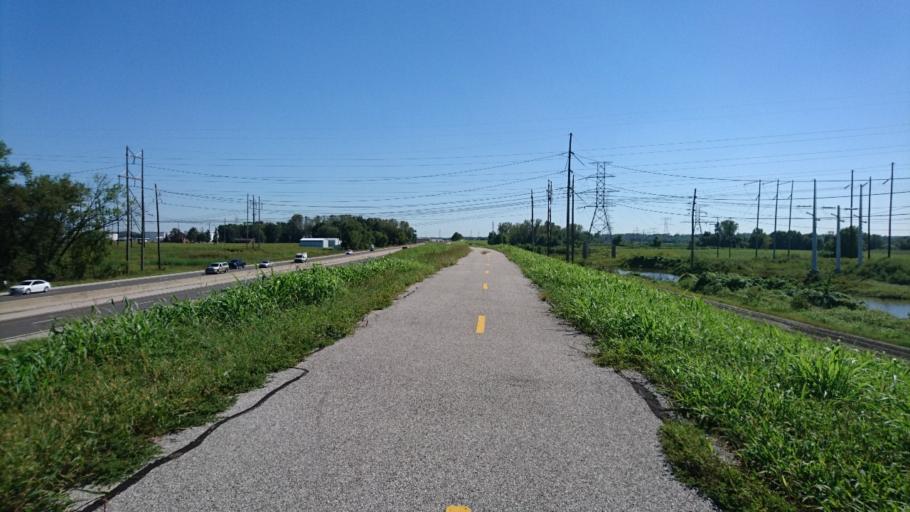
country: US
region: Illinois
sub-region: Madison County
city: Hartford
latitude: 38.8268
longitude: -90.1008
